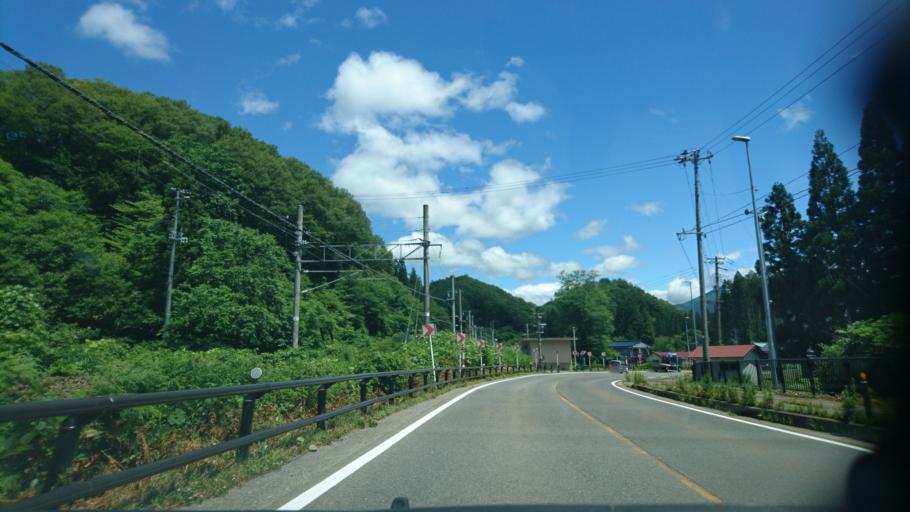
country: JP
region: Akita
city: Kakunodatemachi
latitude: 39.6809
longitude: 140.7037
